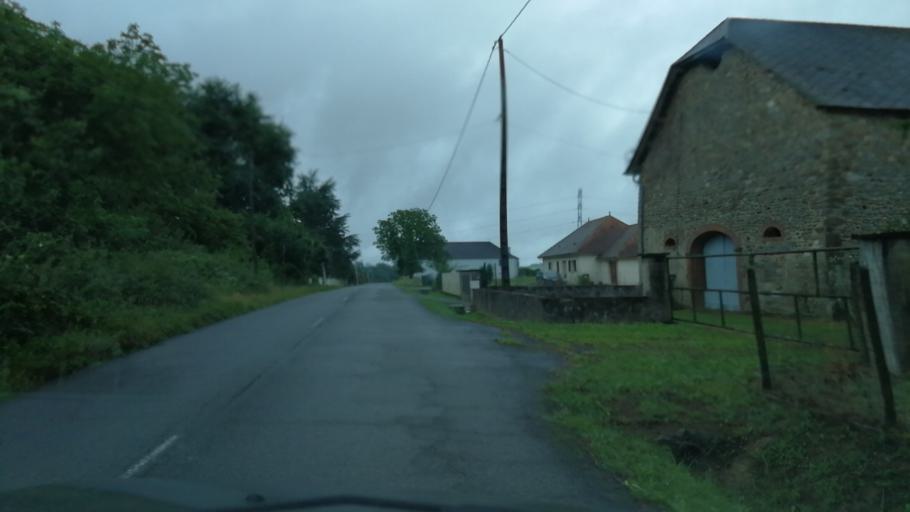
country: FR
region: Aquitaine
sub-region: Departement des Pyrenees-Atlantiques
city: Lucq-de-Bearn
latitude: 43.2920
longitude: -0.6765
